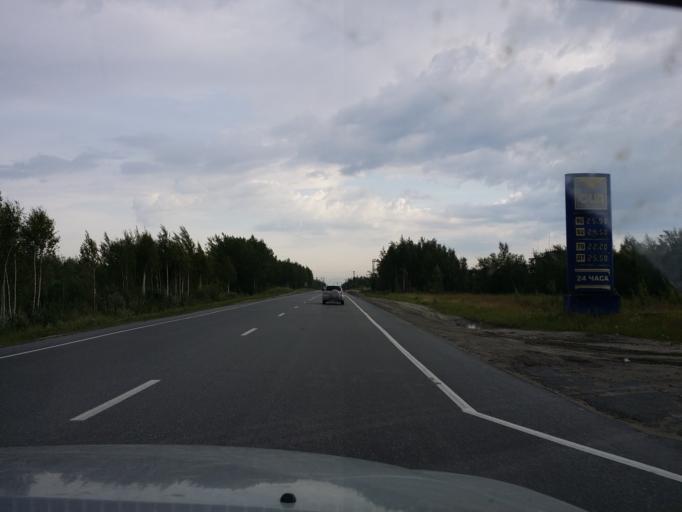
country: RU
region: Khanty-Mansiyskiy Avtonomnyy Okrug
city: Megion
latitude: 61.0692
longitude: 76.1159
